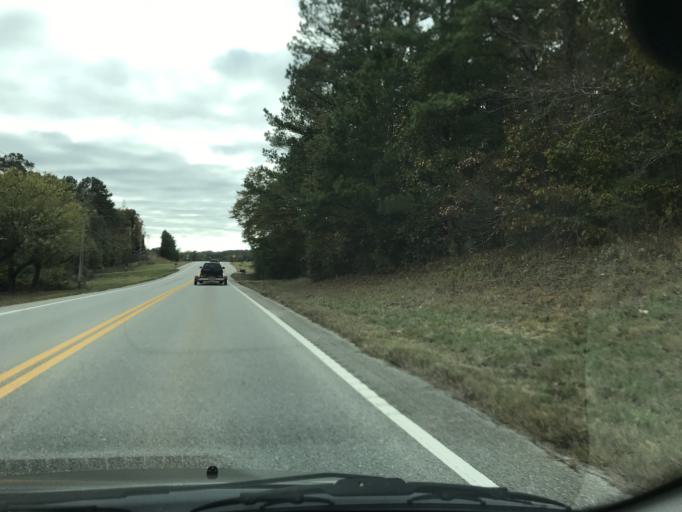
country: US
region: Tennessee
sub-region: Hamilton County
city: Lakesite
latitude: 35.1964
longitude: -85.0451
